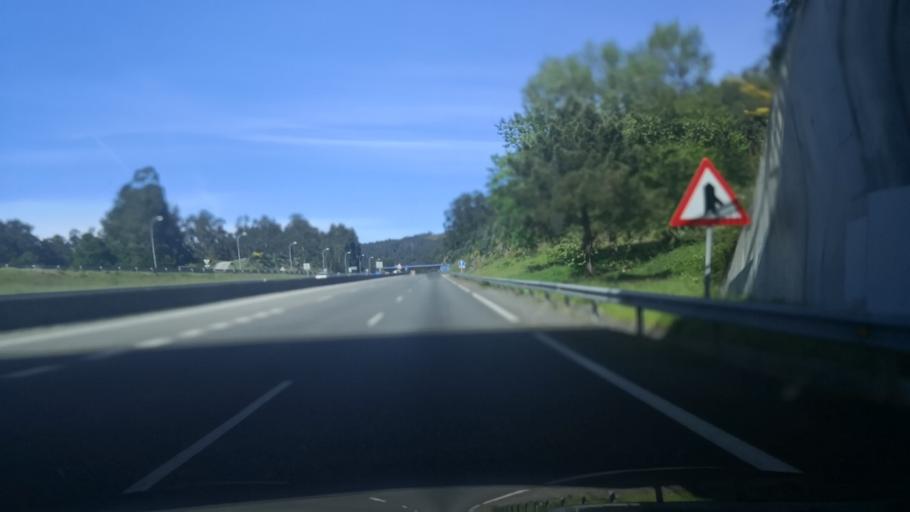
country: ES
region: Galicia
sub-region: Provincia de Pontevedra
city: Meano
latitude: 42.4503
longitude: -8.7851
